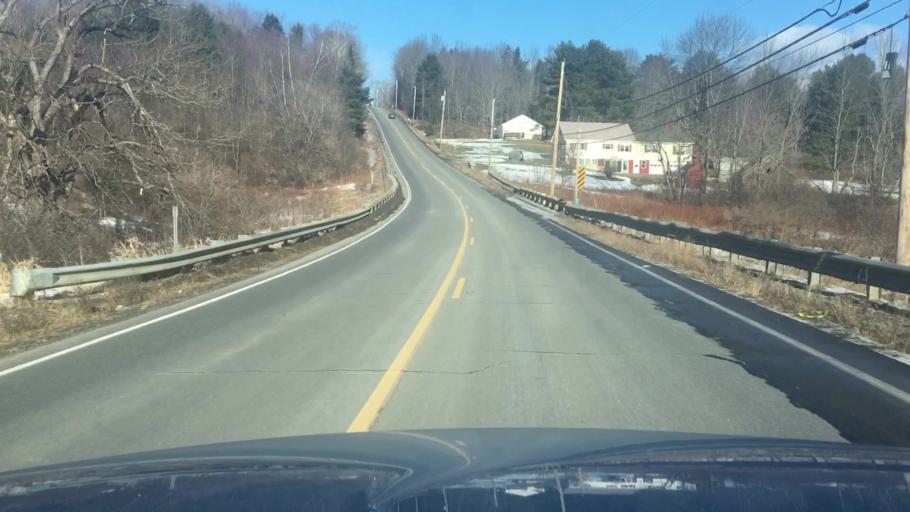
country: US
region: Maine
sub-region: Somerset County
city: Fairfield
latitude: 44.6502
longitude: -69.6760
